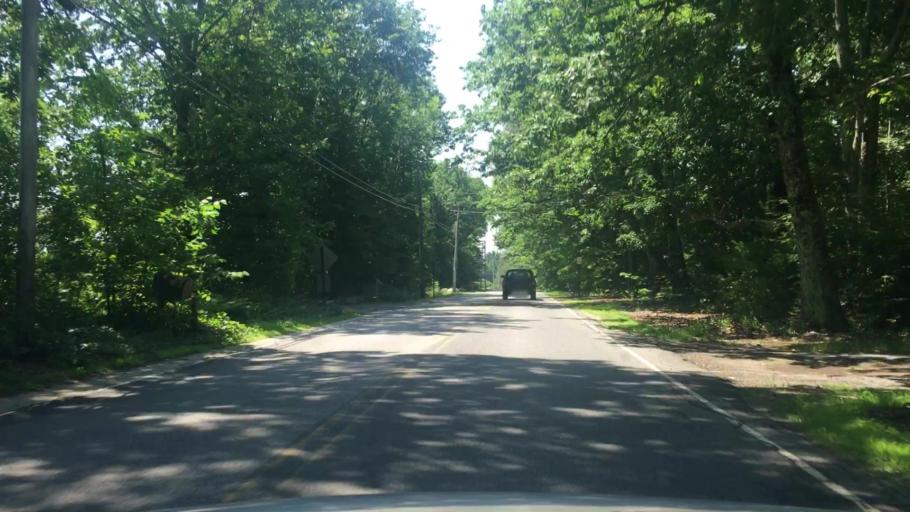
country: US
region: Maine
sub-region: Cumberland County
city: Cumberland Center
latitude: 43.8317
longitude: -70.2983
